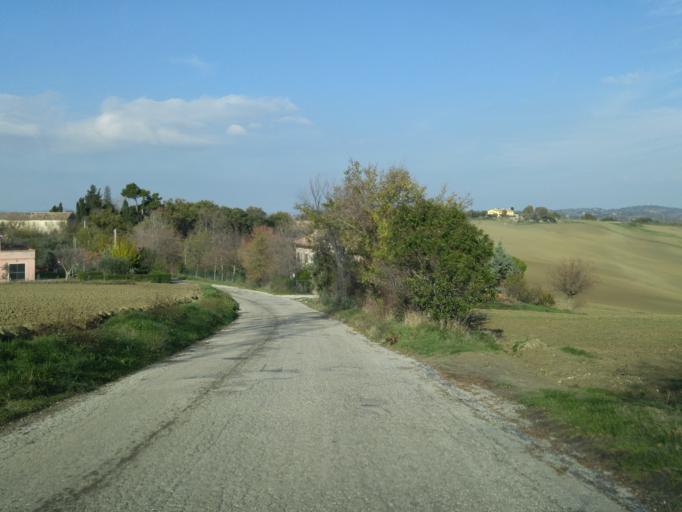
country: IT
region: The Marches
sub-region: Provincia di Pesaro e Urbino
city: Lucrezia
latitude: 43.8088
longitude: 12.9117
